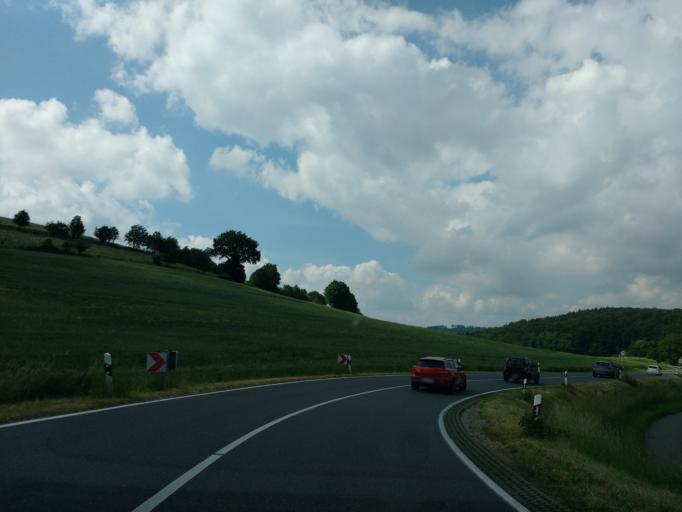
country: DE
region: North Rhine-Westphalia
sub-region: Regierungsbezirk Detmold
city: Lemgo
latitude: 52.0884
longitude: 8.9334
